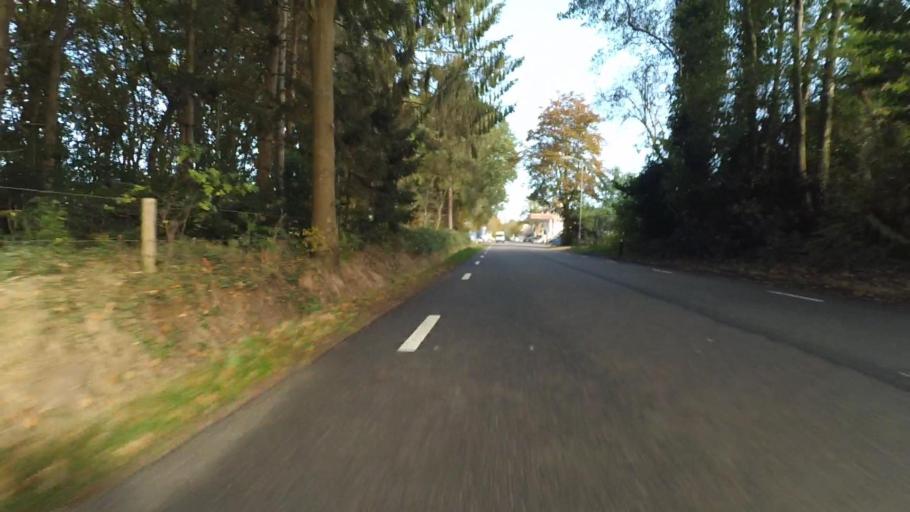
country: NL
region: Gelderland
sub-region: Gemeente Ermelo
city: Horst
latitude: 52.3095
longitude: 5.5919
